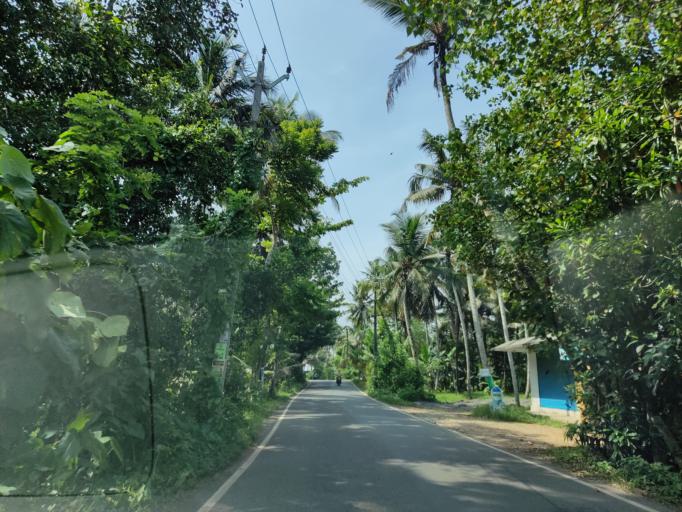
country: IN
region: Kerala
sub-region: Alappuzha
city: Mavelikara
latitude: 9.3351
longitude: 76.4686
